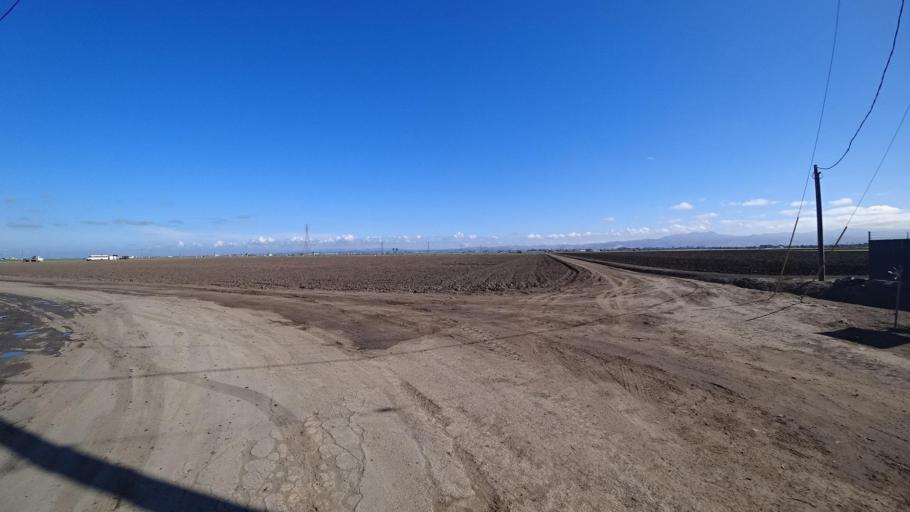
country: US
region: California
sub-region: Monterey County
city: Boronda
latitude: 36.6648
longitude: -121.7025
